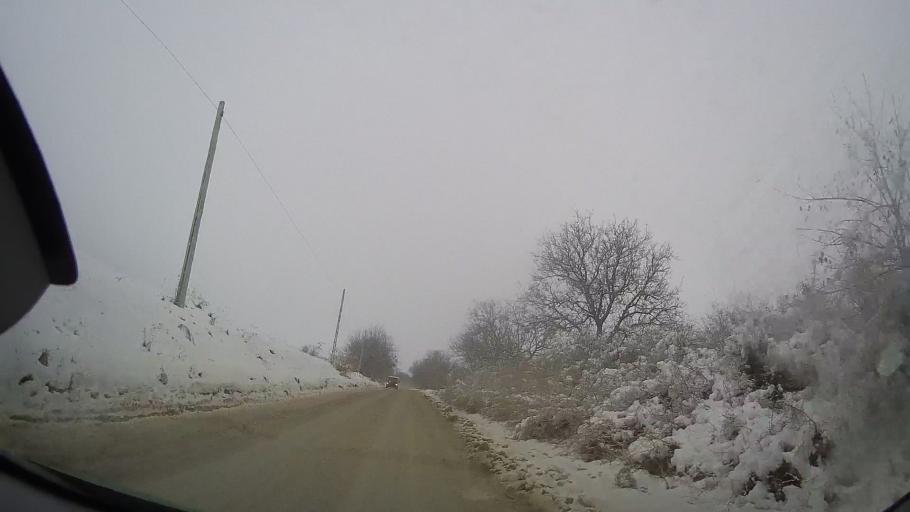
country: RO
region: Vaslui
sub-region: Comuna Todiresti
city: Todiresti
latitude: 46.8731
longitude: 27.3803
